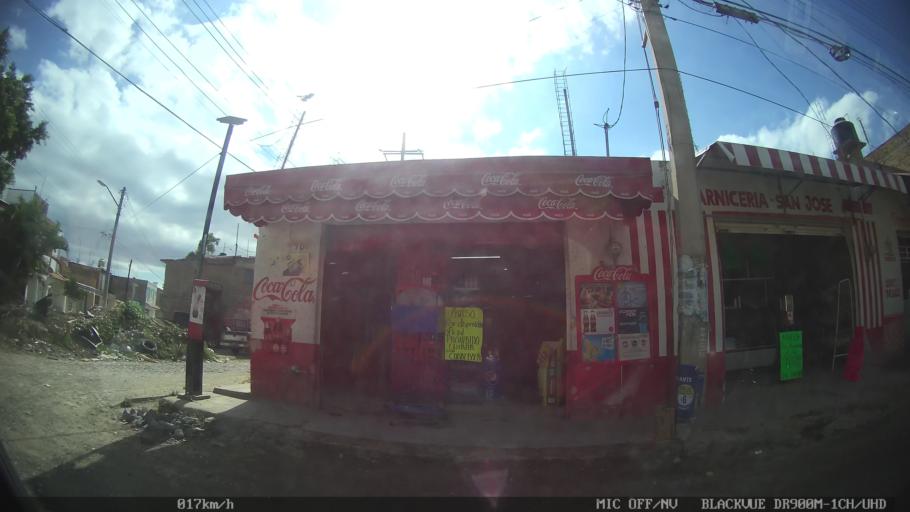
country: MX
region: Jalisco
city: Tonala
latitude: 20.6612
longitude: -103.2529
